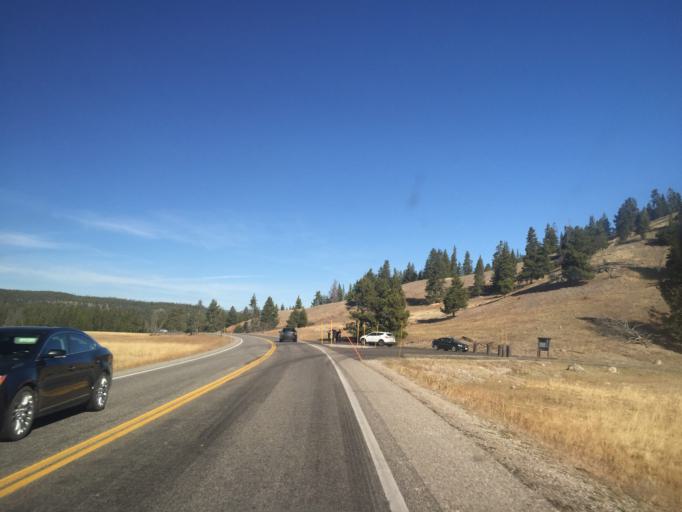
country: US
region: Montana
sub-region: Gallatin County
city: West Yellowstone
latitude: 44.5693
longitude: -110.8159
